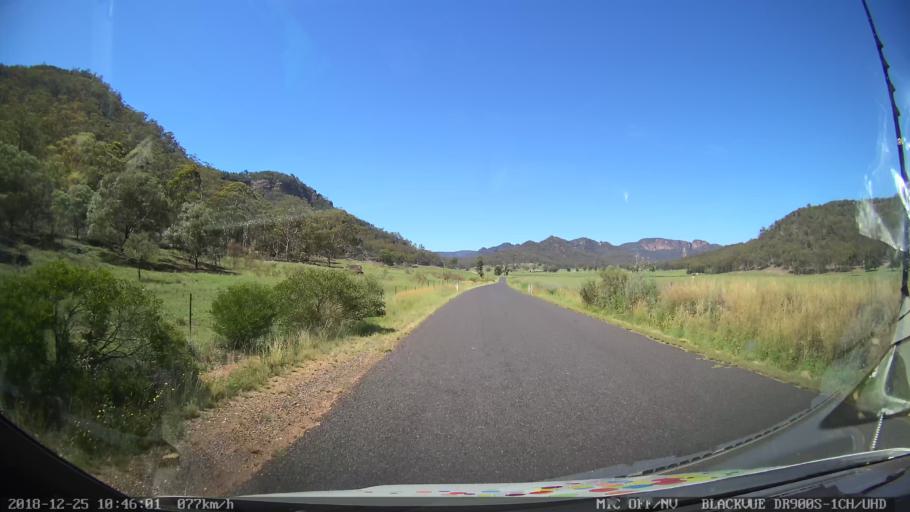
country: AU
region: New South Wales
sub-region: Upper Hunter Shire
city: Merriwa
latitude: -32.4397
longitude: 150.2871
